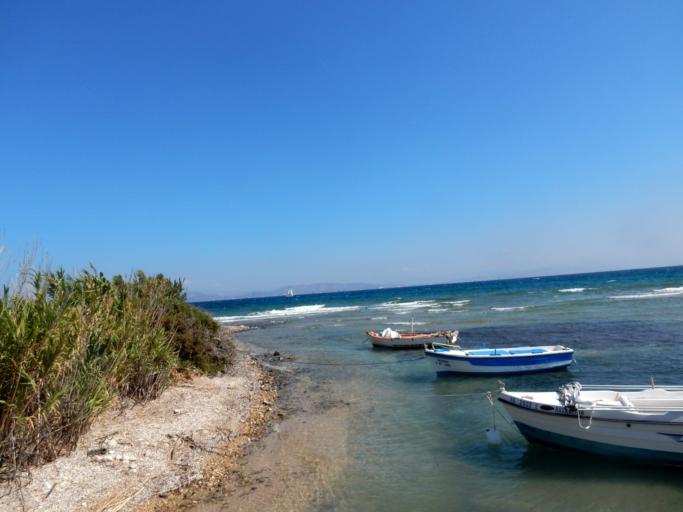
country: GR
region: Attica
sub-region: Nomos Piraios
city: Vathi
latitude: 37.7712
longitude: 23.5353
